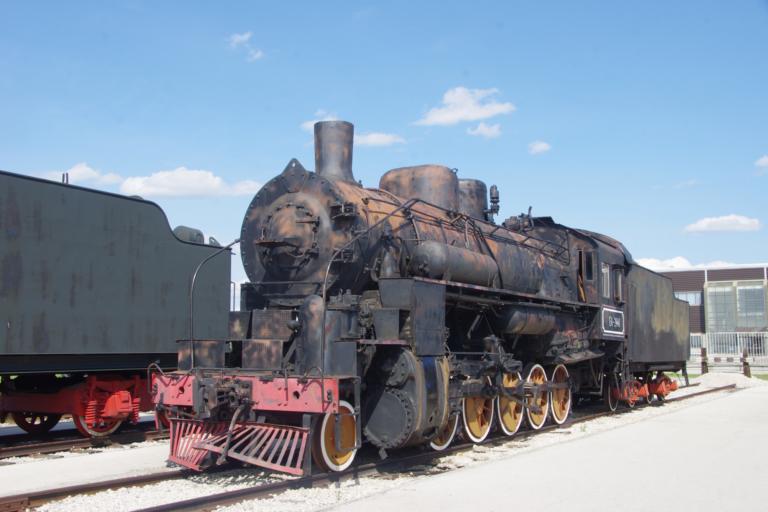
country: RU
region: Samara
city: Tol'yatti
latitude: 53.5514
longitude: 49.2586
